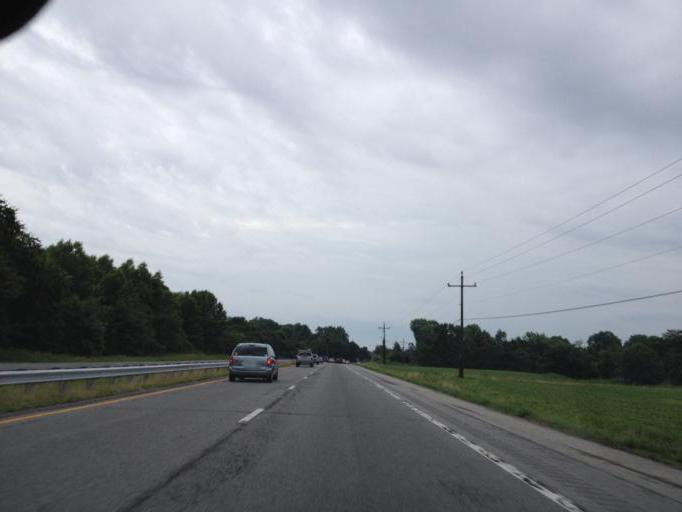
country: US
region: Maryland
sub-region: Queen Anne's County
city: Grasonville
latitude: 38.9767
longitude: -76.1317
